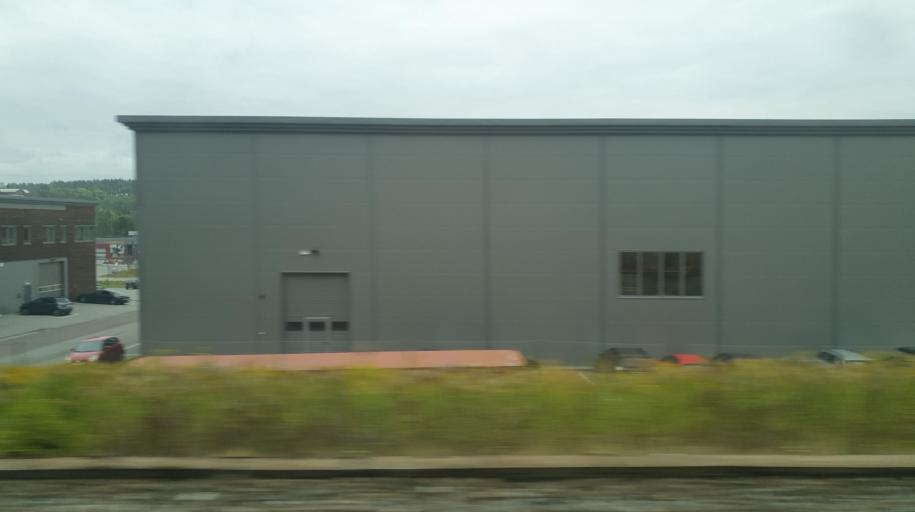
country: NO
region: Buskerud
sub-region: Drammen
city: Skoger
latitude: 59.6906
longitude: 10.2426
